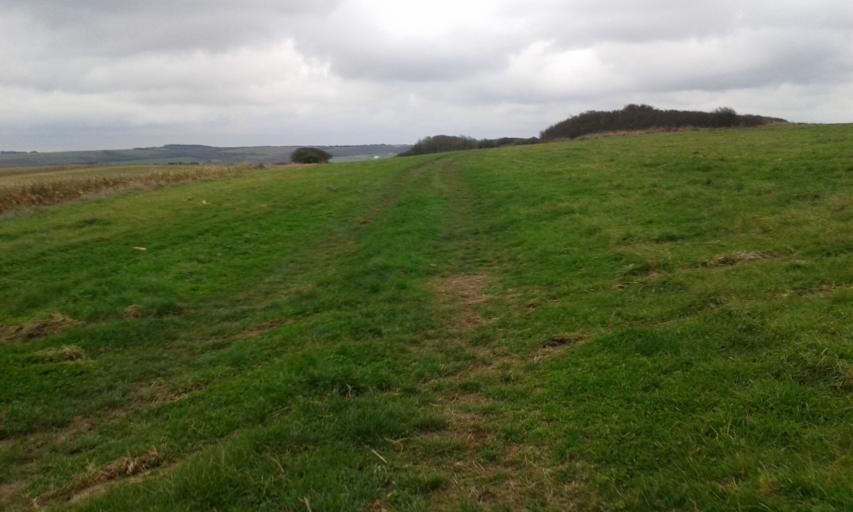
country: FR
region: Nord-Pas-de-Calais
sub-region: Departement du Pas-de-Calais
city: Wissant
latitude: 50.8965
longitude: 1.7119
